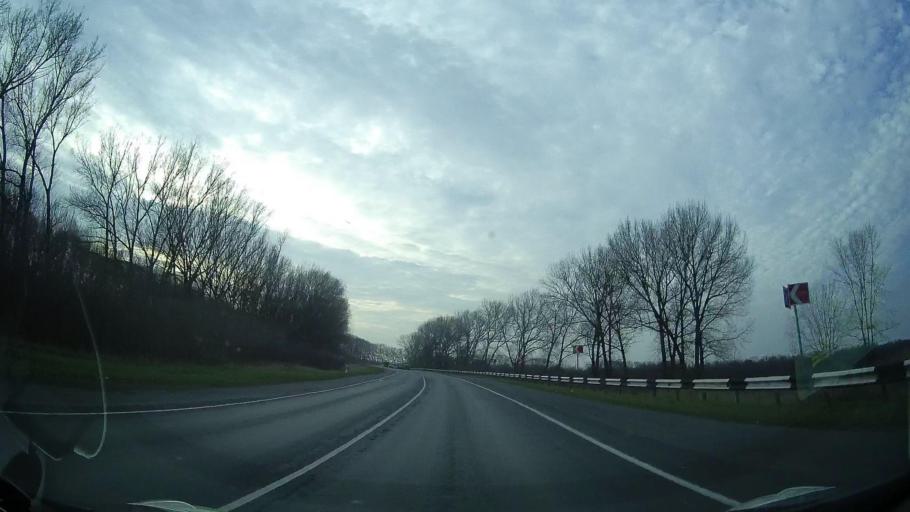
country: RU
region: Rostov
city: Starocherkasskaya
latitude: 47.1555
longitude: 40.1875
